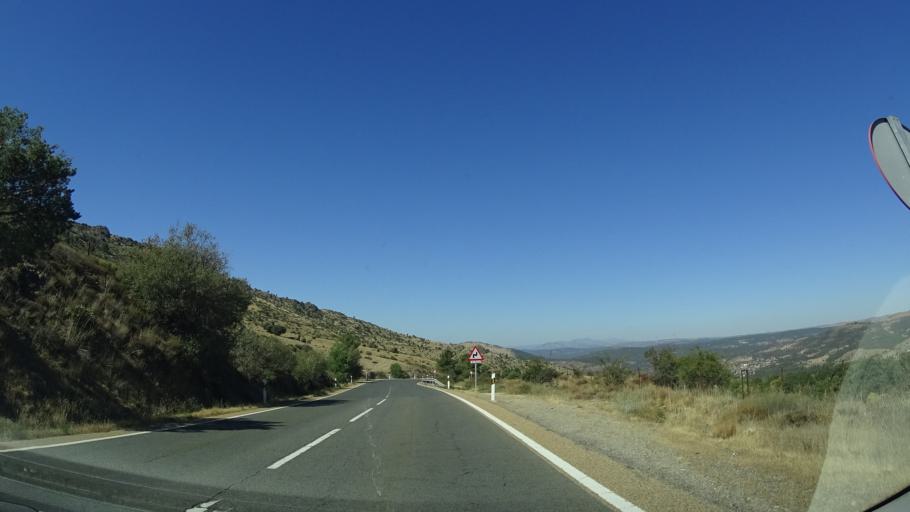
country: ES
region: Madrid
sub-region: Provincia de Madrid
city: Zarzalejo
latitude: 40.5637
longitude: -4.2140
